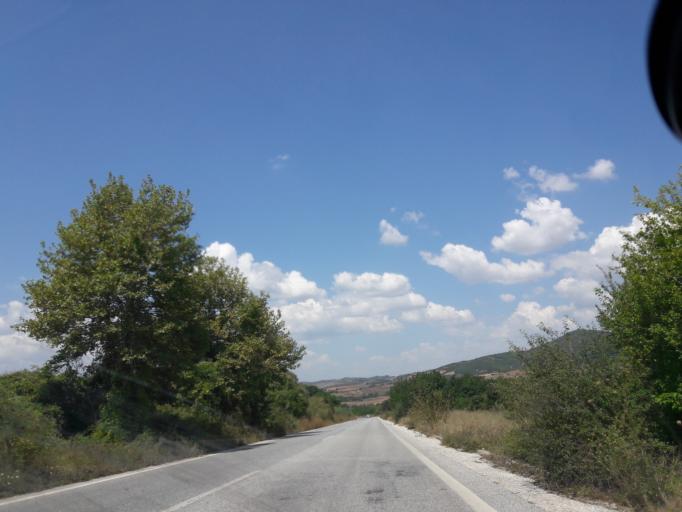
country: GR
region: Central Macedonia
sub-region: Nomos Chalkidikis
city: Polygyros
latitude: 40.4586
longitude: 23.4019
